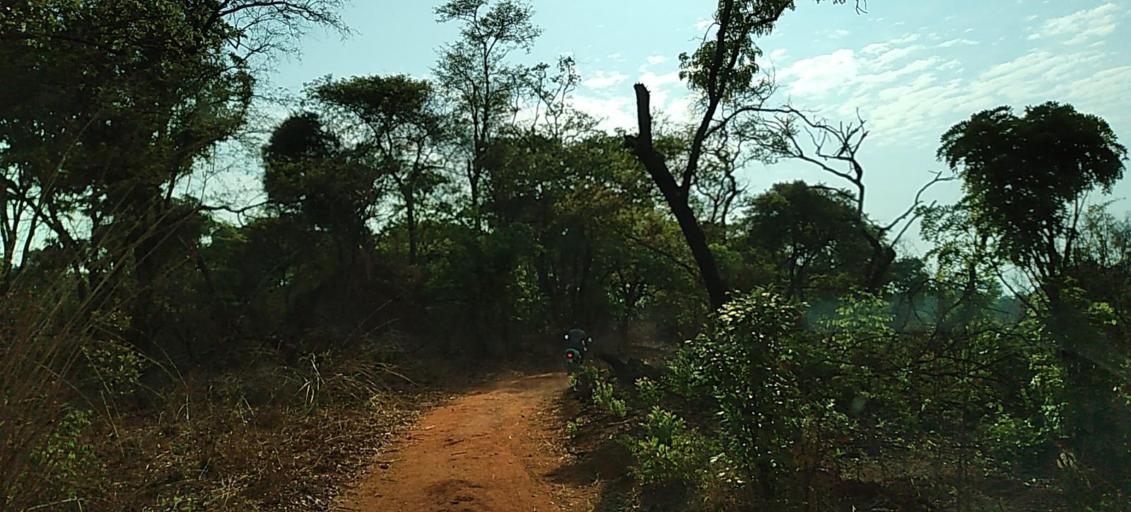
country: ZM
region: Copperbelt
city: Kalulushi
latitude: -12.9629
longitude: 27.7089
